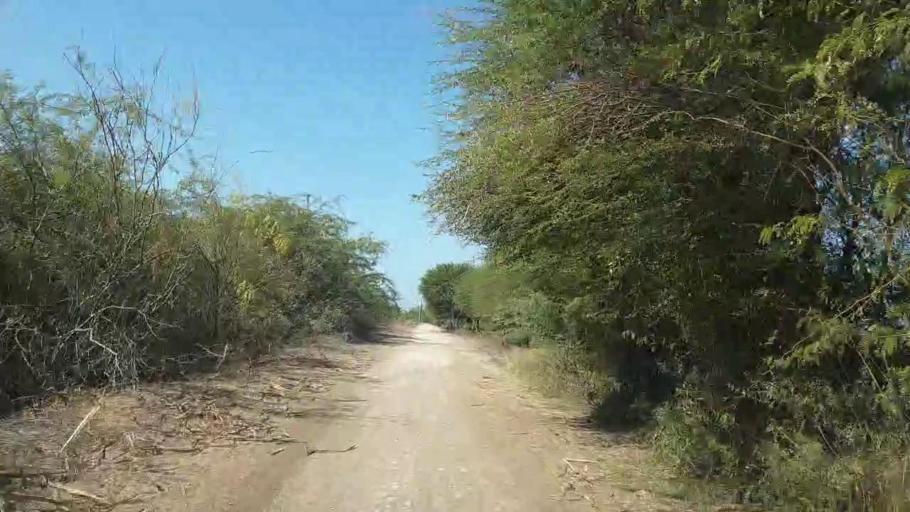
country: PK
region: Sindh
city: Mirpur Khas
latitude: 25.6142
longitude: 69.1384
